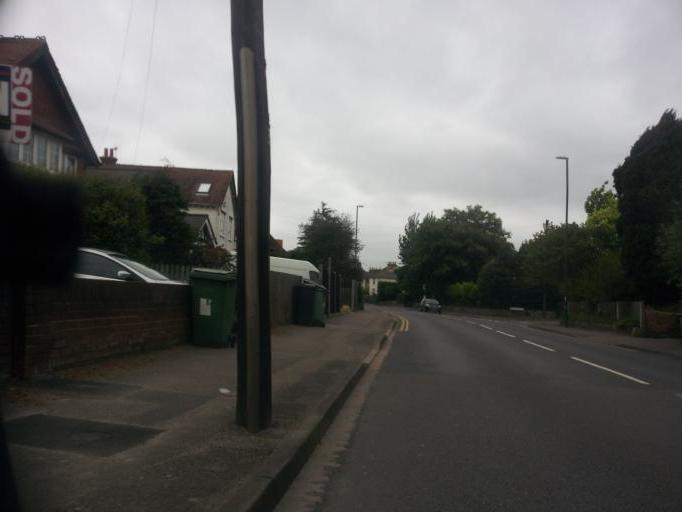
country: GB
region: England
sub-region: Kent
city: Maidstone
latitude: 51.2466
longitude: 0.5247
